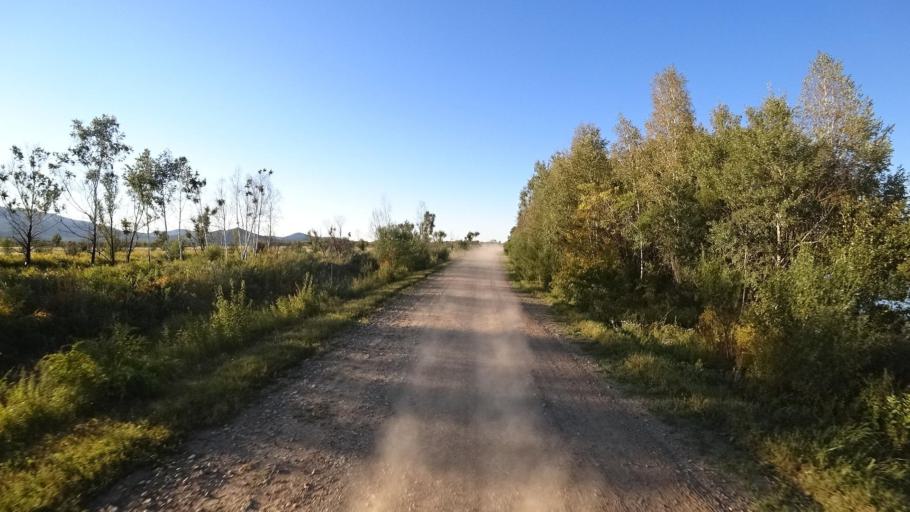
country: RU
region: Primorskiy
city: Kirovskiy
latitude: 44.8088
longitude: 133.6168
